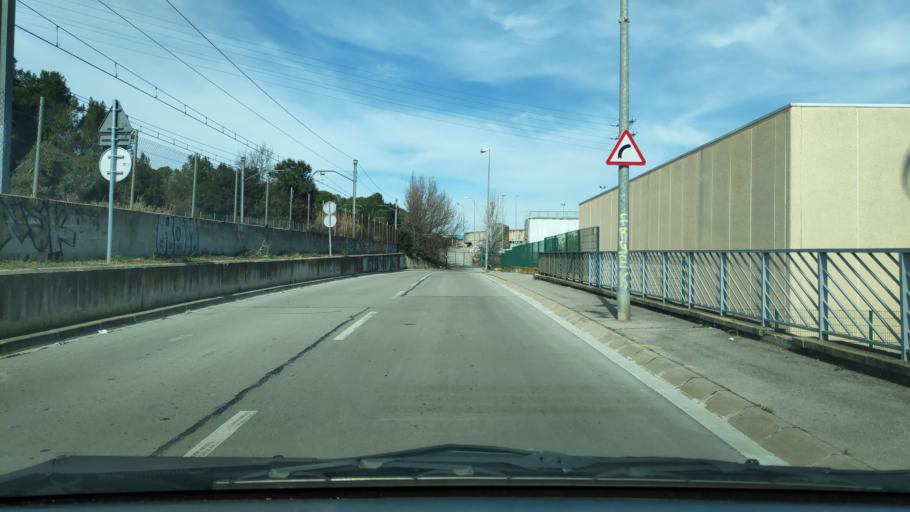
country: ES
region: Catalonia
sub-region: Provincia de Barcelona
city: Rubi
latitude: 41.5114
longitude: 2.0321
